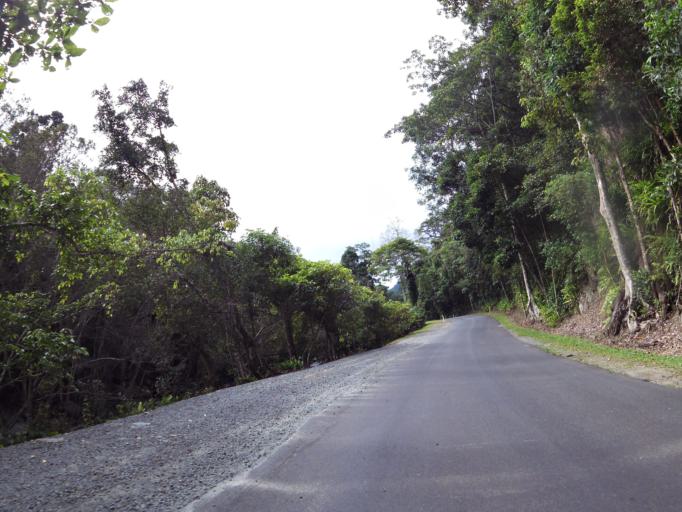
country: AU
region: Queensland
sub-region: Cairns
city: Woree
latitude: -16.9597
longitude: 145.6825
